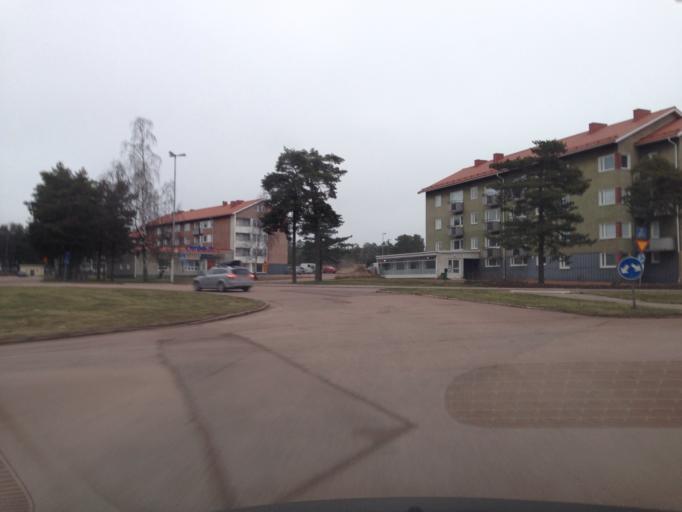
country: AX
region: Mariehamns stad
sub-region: Mariehamn
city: Mariehamn
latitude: 60.1044
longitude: 19.9372
